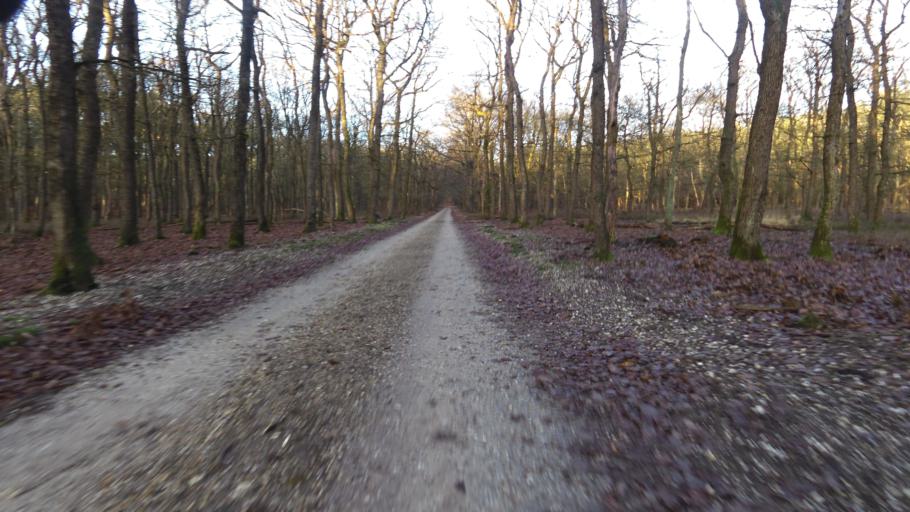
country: NL
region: Gelderland
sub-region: Gemeente Apeldoorn
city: Uddel
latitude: 52.2182
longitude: 5.8421
